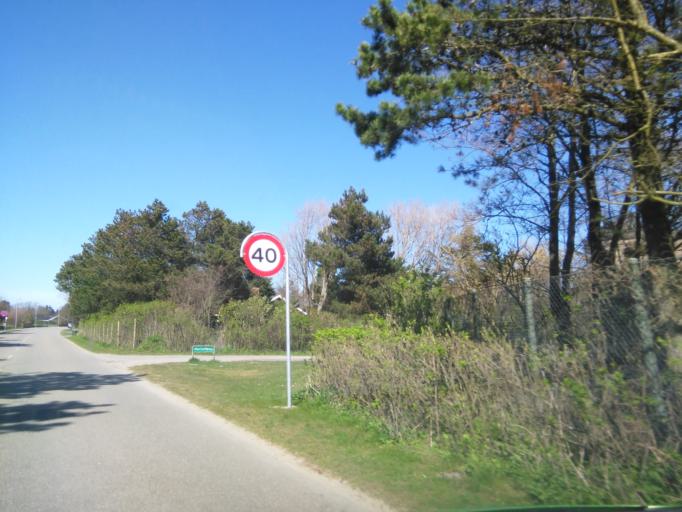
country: DK
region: South Denmark
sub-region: Varde Kommune
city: Oksbol
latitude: 55.5481
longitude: 8.1342
